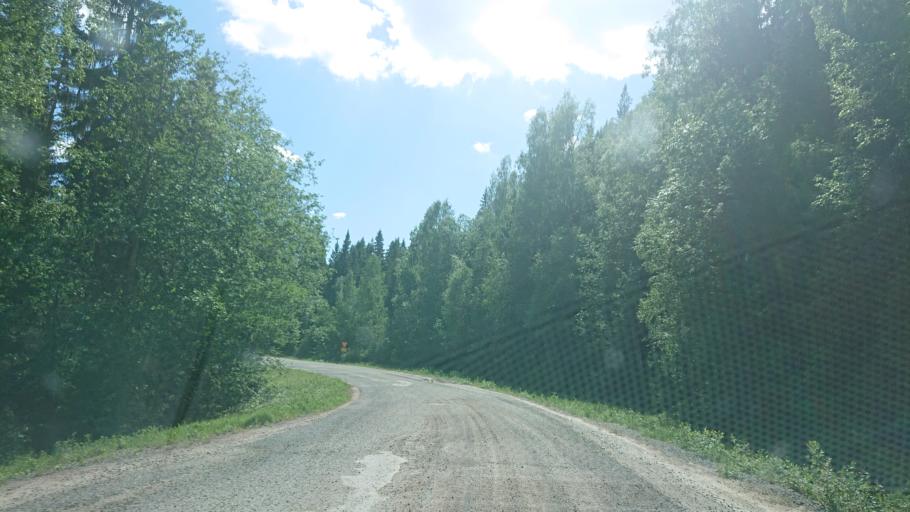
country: SE
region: Vaesternorrland
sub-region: Solleftea Kommun
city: Solleftea
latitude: 62.9678
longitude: 17.1821
